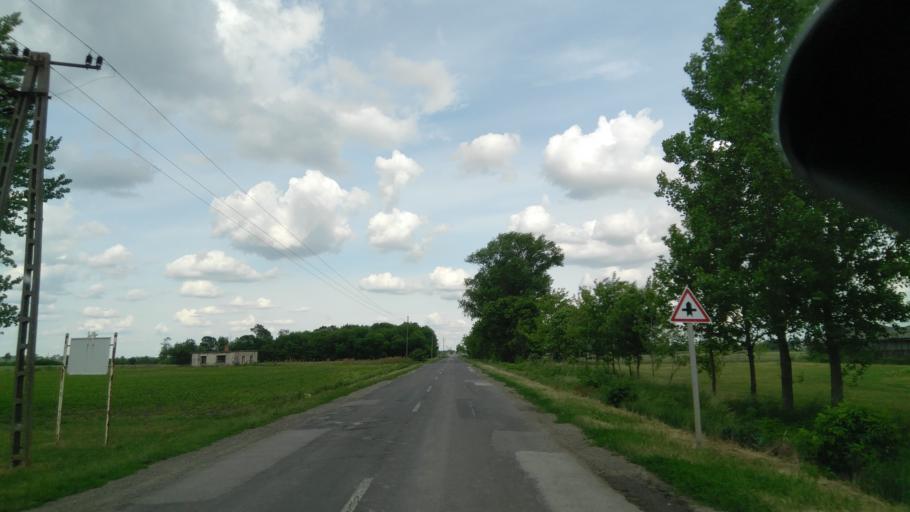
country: HU
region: Bekes
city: Battonya
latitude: 46.2937
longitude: 20.9804
